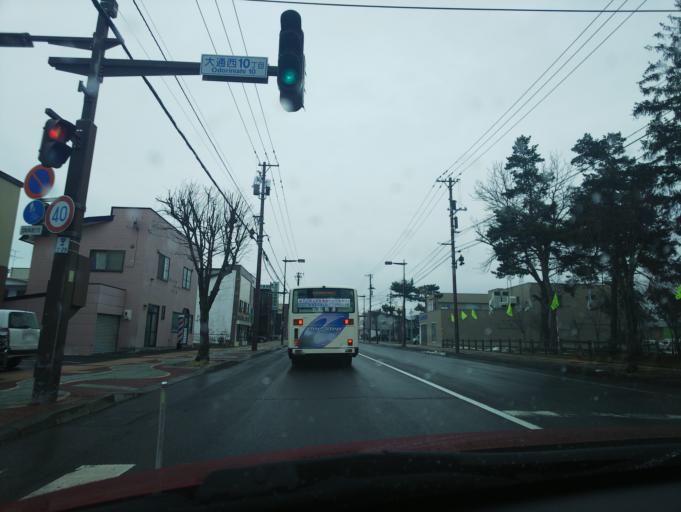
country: JP
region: Hokkaido
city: Nayoro
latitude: 44.1711
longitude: 142.3938
